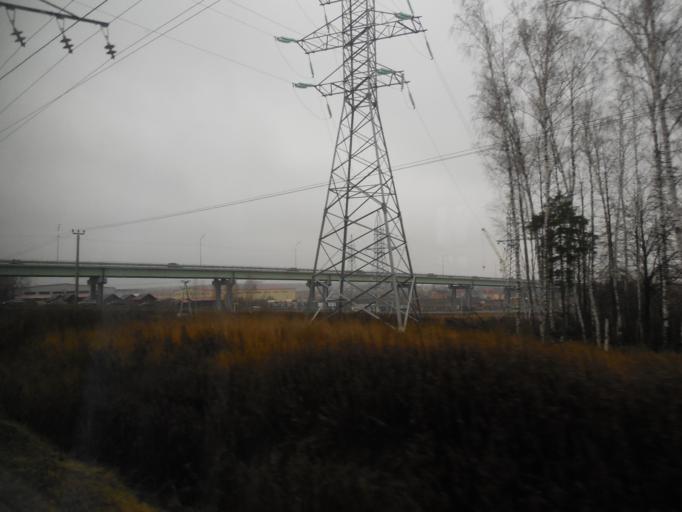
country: RU
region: Moskovskaya
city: Belyye Stolby
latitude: 55.3443
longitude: 37.8426
